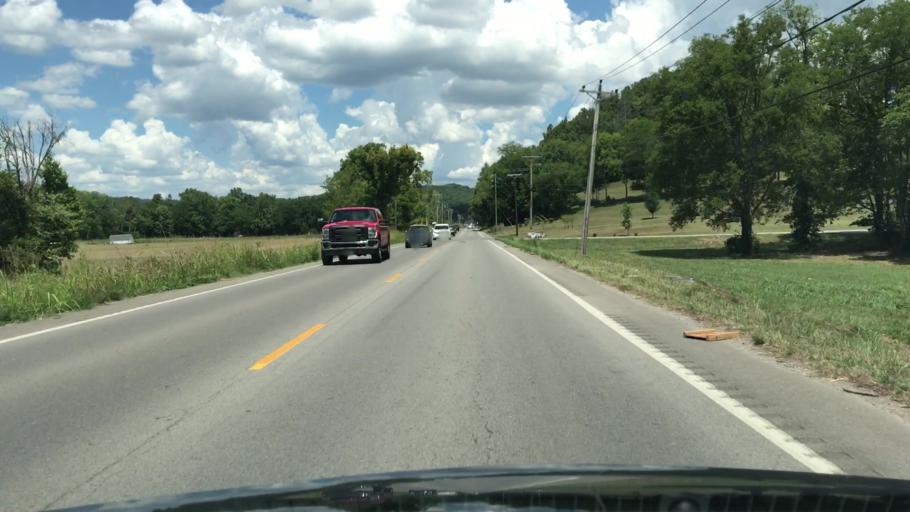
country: US
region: Tennessee
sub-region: Williamson County
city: Nolensville
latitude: 35.8852
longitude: -86.6631
